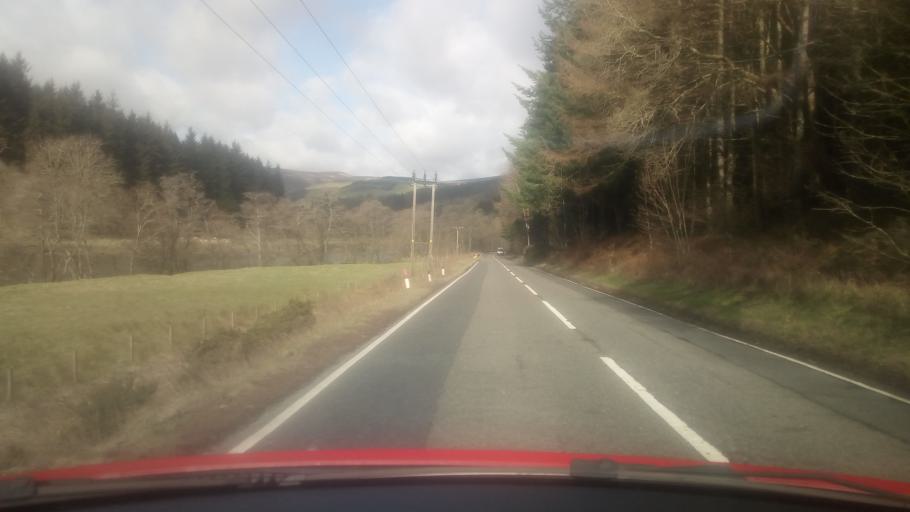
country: GB
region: Scotland
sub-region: The Scottish Borders
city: Innerleithen
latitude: 55.6201
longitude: -2.9554
